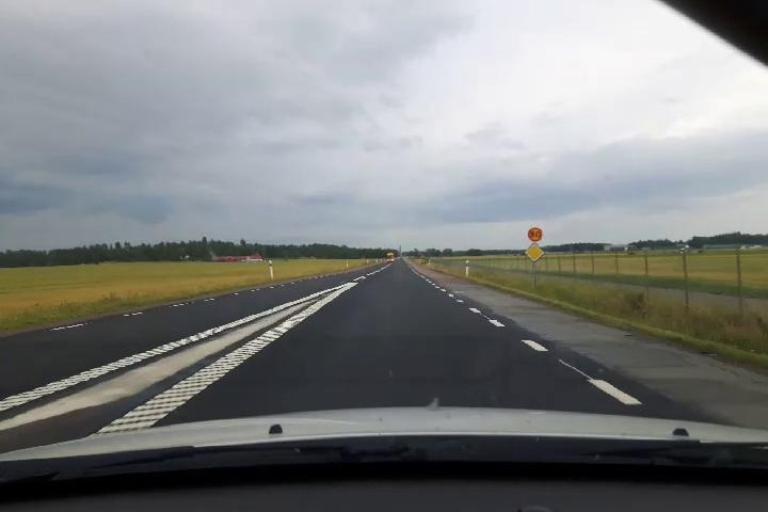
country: SE
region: Uppsala
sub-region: Uppsala Kommun
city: Gamla Uppsala
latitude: 59.8978
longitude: 17.6135
